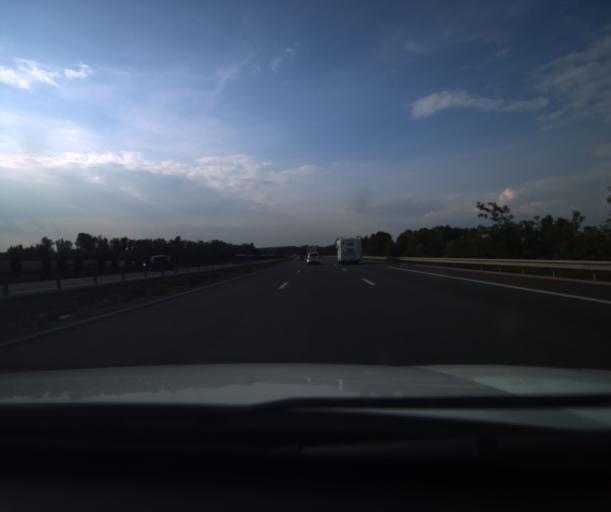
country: FR
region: Midi-Pyrenees
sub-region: Departement du Tarn-et-Garonne
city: Campsas
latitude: 43.9173
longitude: 1.3185
